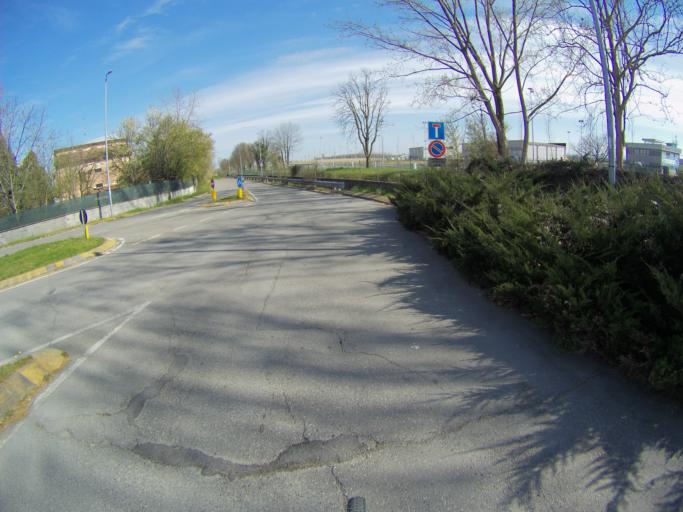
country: IT
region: Emilia-Romagna
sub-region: Provincia di Reggio Emilia
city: Reggio nell'Emilia
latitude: 44.7025
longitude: 10.6653
